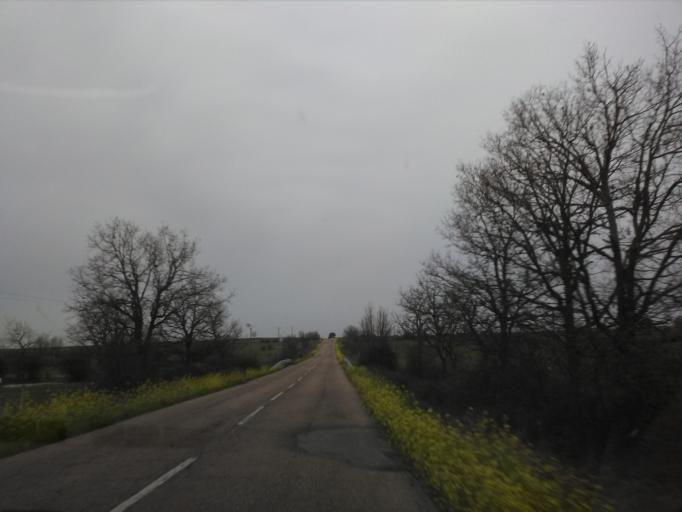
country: ES
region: Castille and Leon
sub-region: Provincia de Salamanca
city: Moronta
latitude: 40.9846
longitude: -6.4613
